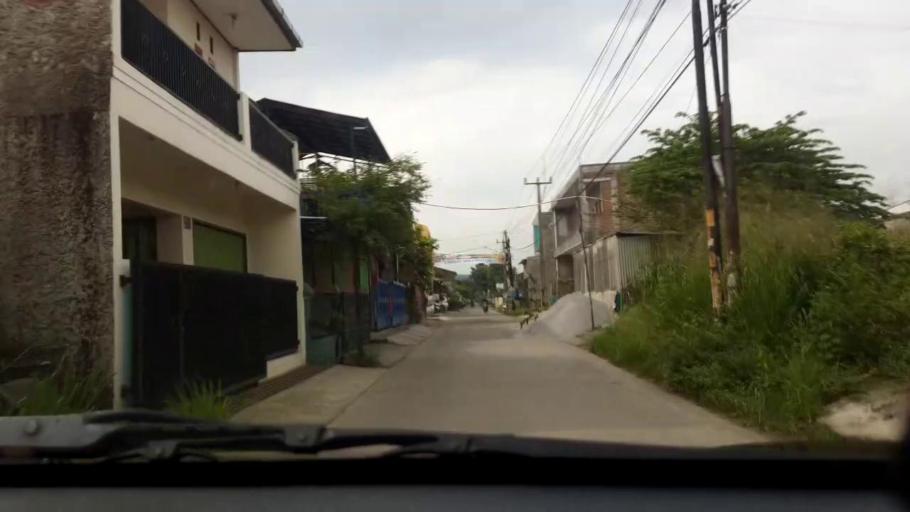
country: ID
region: West Java
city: Cileunyi
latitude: -6.9454
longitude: 107.7210
